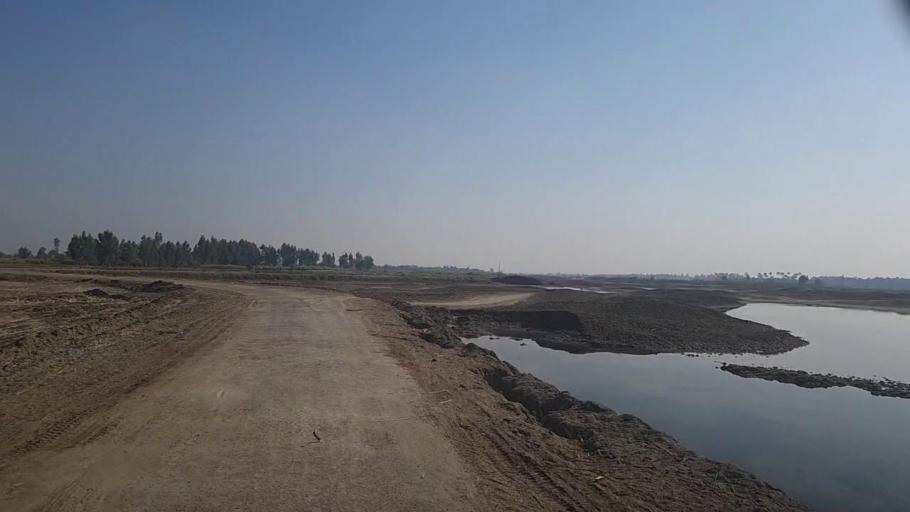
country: PK
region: Sindh
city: Kot Diji
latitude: 27.4341
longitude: 68.7280
